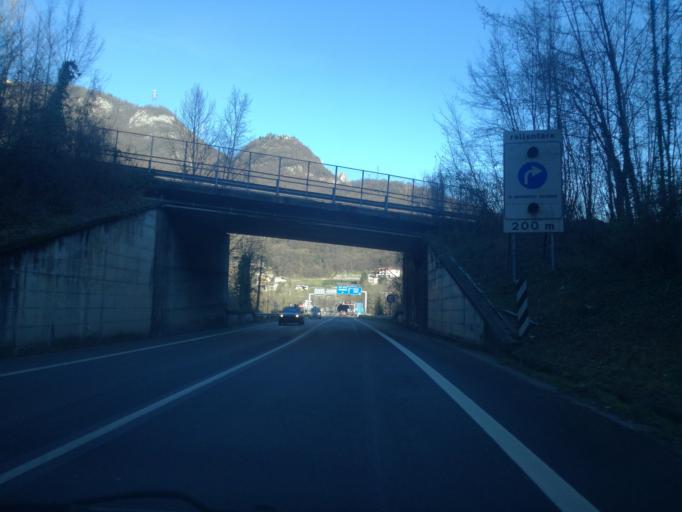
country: IT
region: Lombardy
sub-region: Provincia di Bergamo
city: Pianico
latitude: 45.8082
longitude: 10.0524
